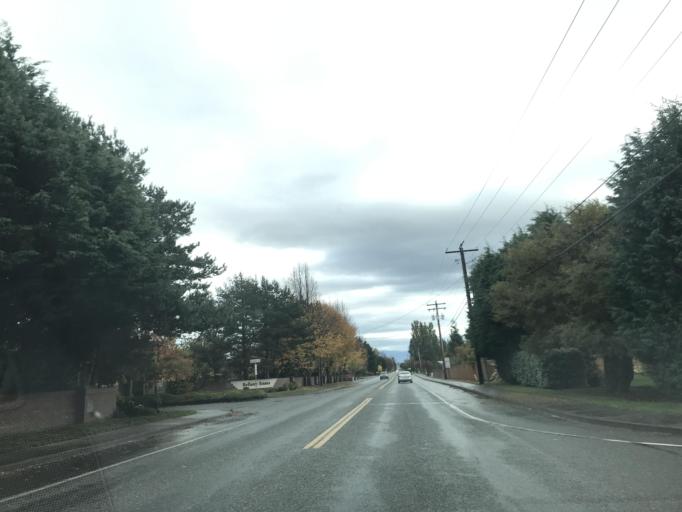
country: US
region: Washington
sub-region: Whatcom County
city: Ferndale
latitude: 48.8334
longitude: -122.5521
